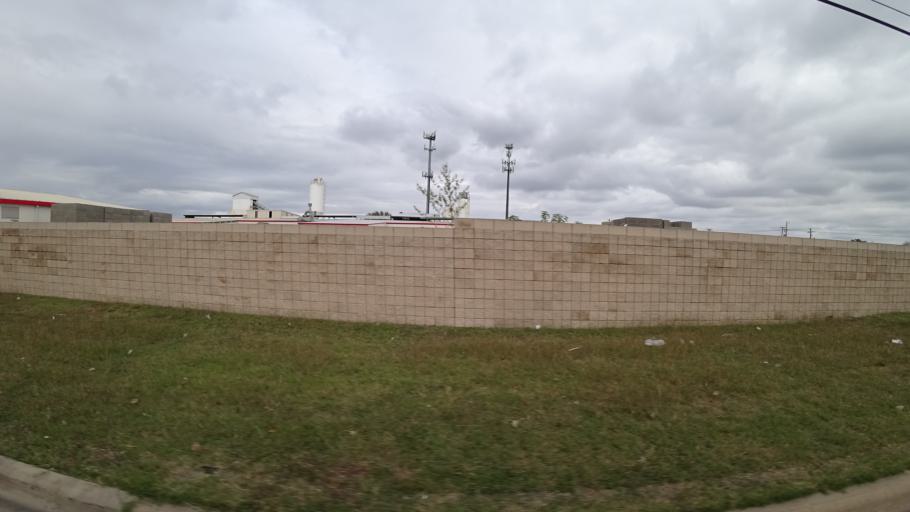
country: US
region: Texas
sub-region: Williamson County
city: Round Rock
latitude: 30.5015
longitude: -97.6861
